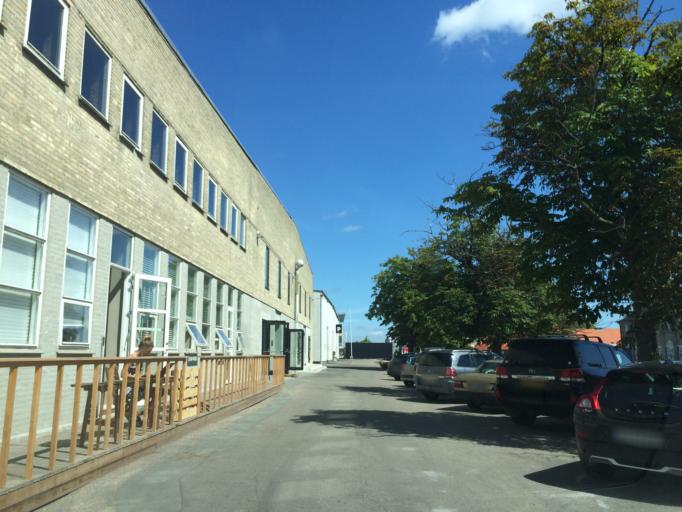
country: DK
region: Capital Region
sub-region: Kobenhavn
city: Christianshavn
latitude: 55.6785
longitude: 12.5990
